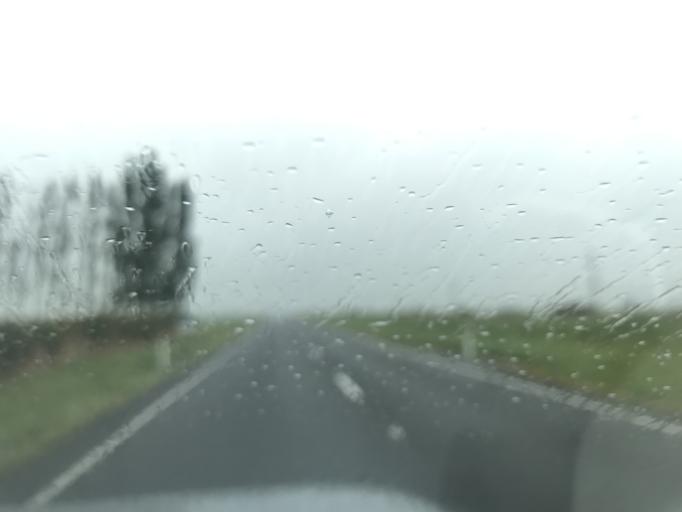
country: NZ
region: Canterbury
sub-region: Selwyn District
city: Darfield
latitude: -43.5056
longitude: 172.2249
